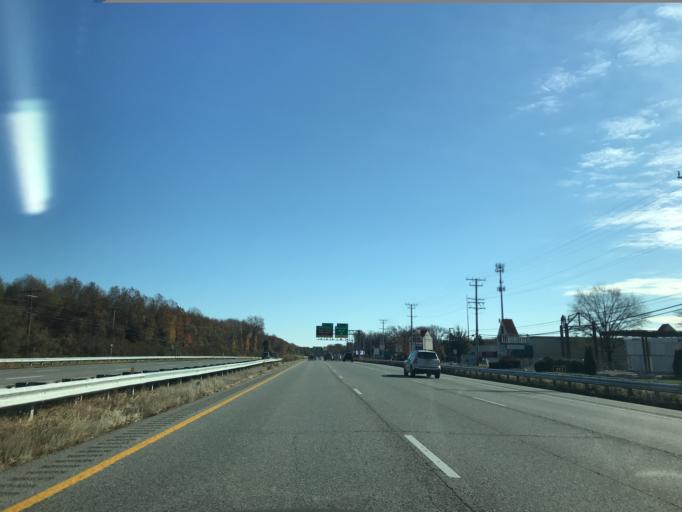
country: US
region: Maryland
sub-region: Anne Arundel County
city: Cape Saint Claire
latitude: 39.0231
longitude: -76.4266
